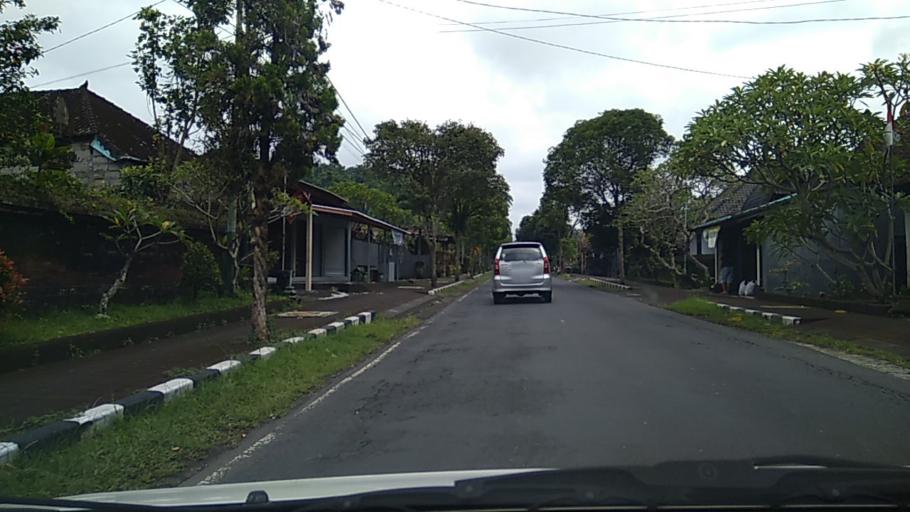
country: ID
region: Bali
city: Brahmana
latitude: -8.4839
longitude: 115.2099
